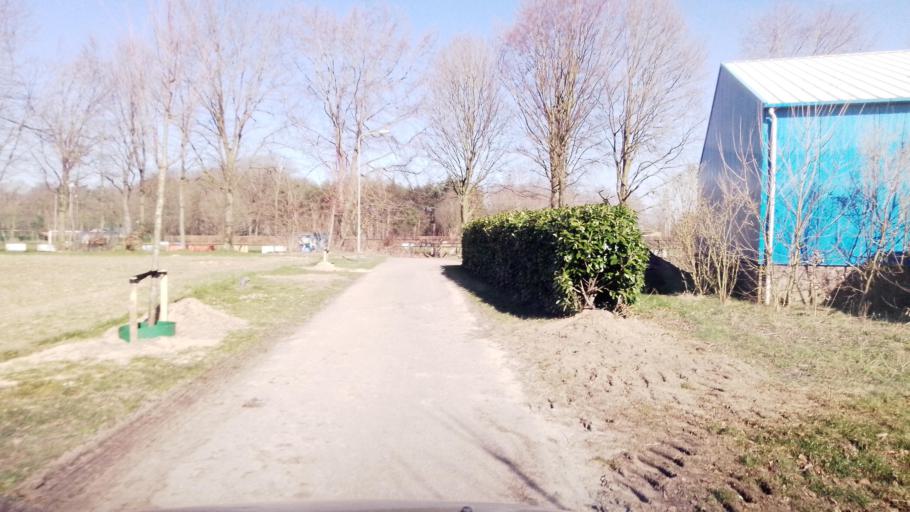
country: NL
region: Limburg
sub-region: Gemeente Venlo
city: Arcen
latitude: 51.4664
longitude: 6.1632
